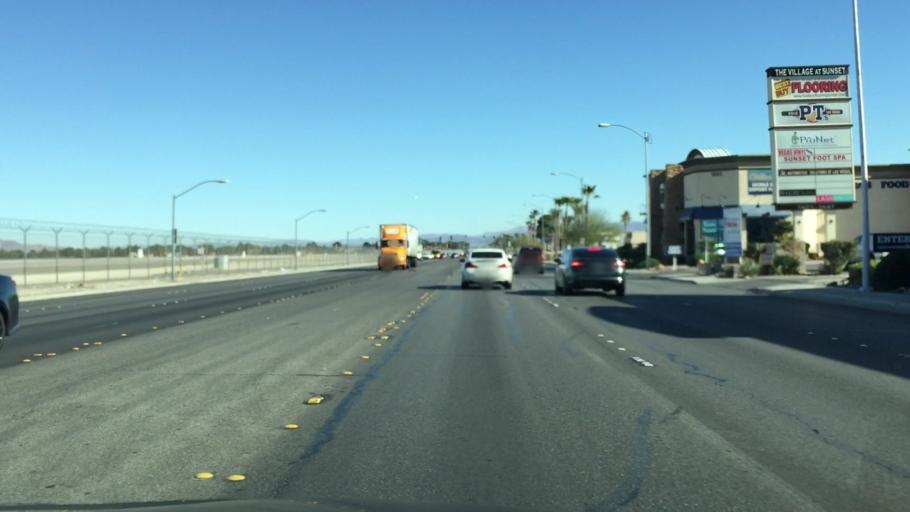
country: US
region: Nevada
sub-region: Clark County
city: Paradise
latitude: 36.0717
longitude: -115.1310
